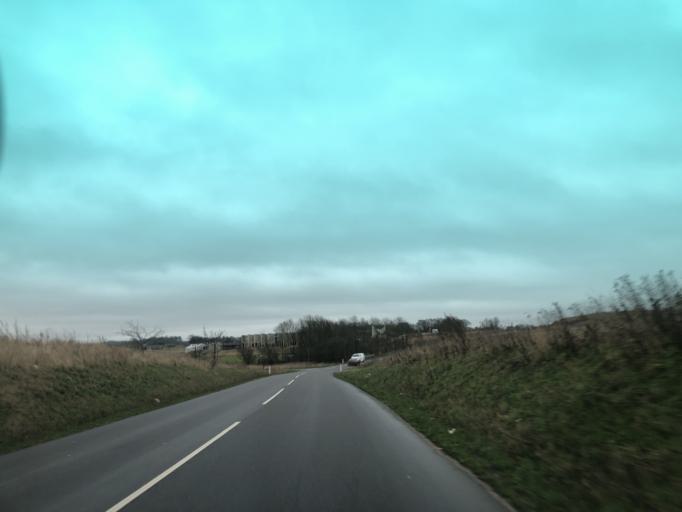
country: DK
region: Central Jutland
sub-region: Randers Kommune
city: Randers
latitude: 56.4222
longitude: 10.0677
